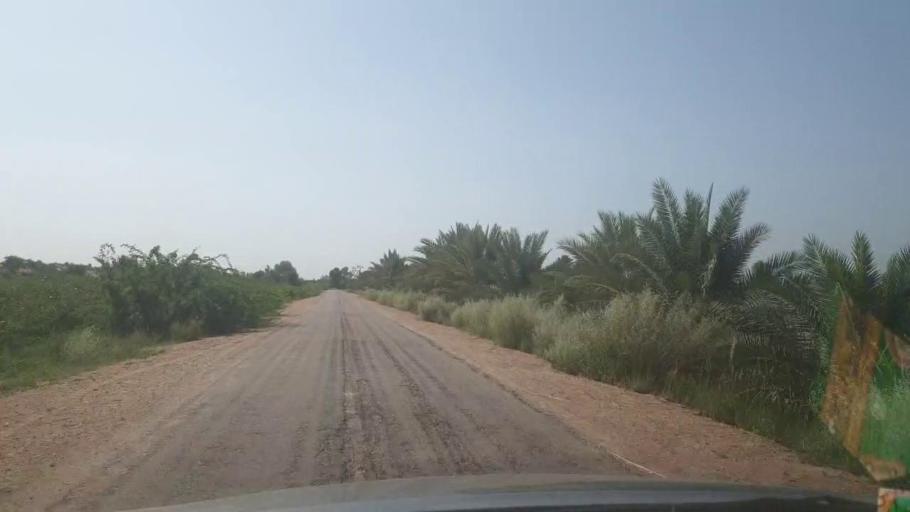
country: PK
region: Sindh
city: Rohri
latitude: 27.4634
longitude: 69.0405
